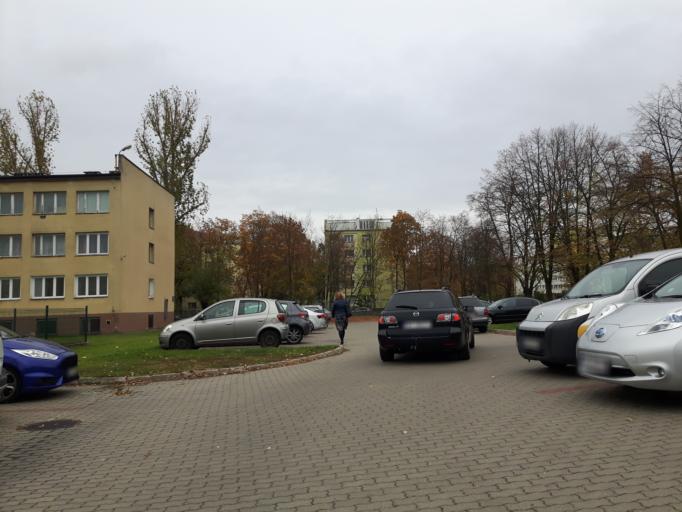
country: PL
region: Masovian Voivodeship
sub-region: Warszawa
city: Praga Poludnie
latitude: 52.2504
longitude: 21.0914
